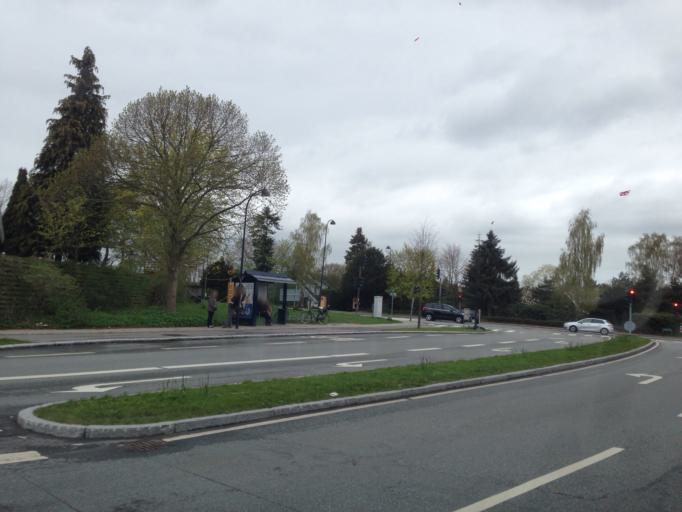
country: DK
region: Capital Region
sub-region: Rudersdal Kommune
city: Trorod
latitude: 55.8456
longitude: 12.5333
